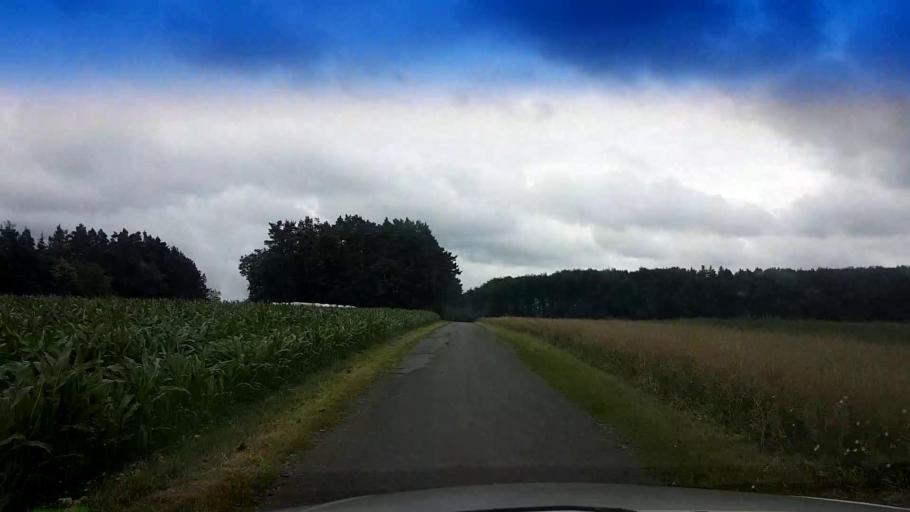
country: DE
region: Bavaria
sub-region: Upper Franconia
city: Poxdorf
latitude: 49.9016
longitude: 11.0811
